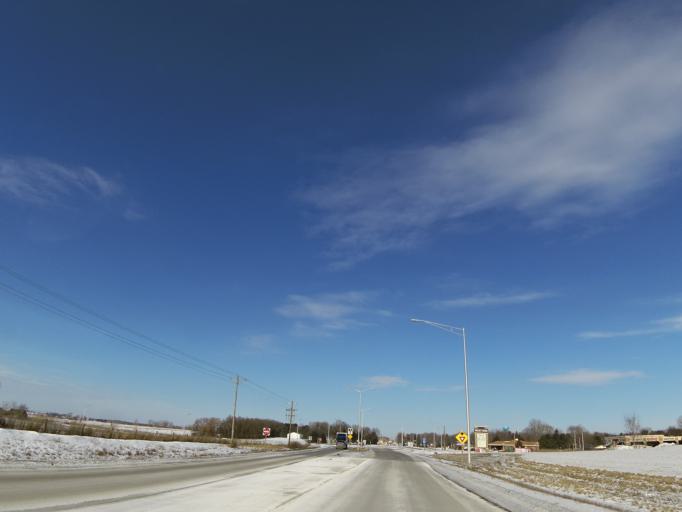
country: US
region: Wisconsin
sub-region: Saint Croix County
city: Roberts
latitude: 44.9759
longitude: -92.5581
